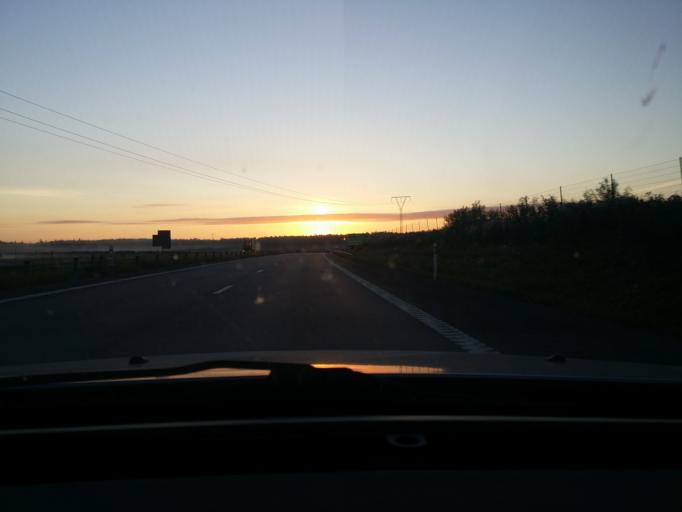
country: SE
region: Uppsala
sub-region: Enkopings Kommun
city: Hummelsta
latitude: 59.6327
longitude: 16.8503
